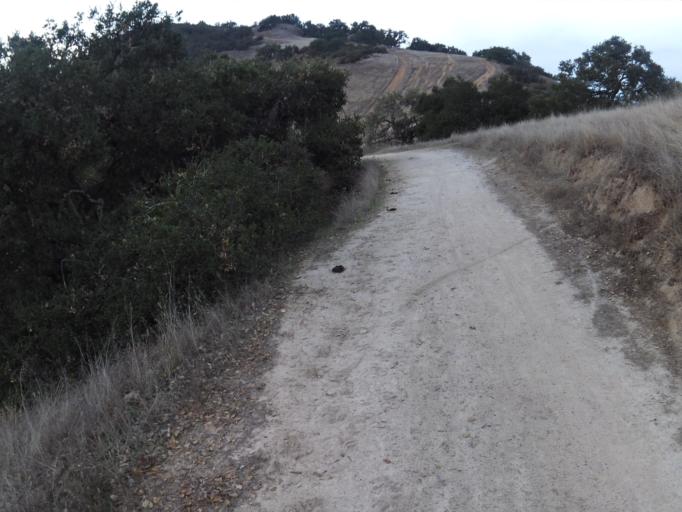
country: US
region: California
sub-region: Monterey County
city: Salinas
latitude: 36.5718
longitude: -121.6682
